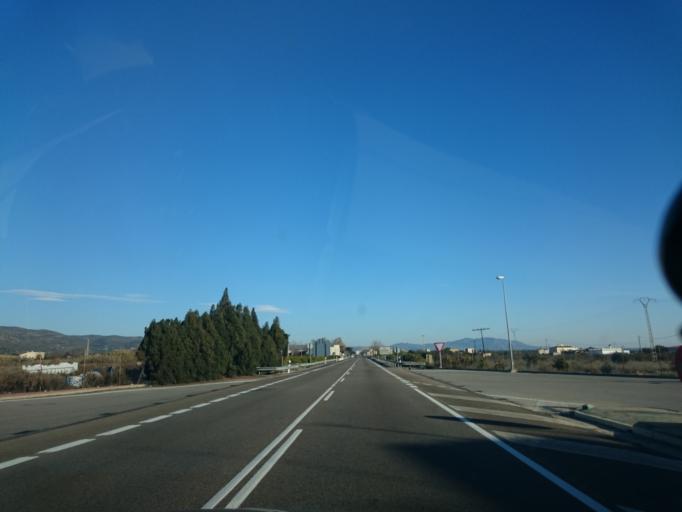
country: ES
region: Valencia
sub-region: Provincia de Castello
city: Orpesa/Oropesa del Mar
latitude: 40.1354
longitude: 0.1497
